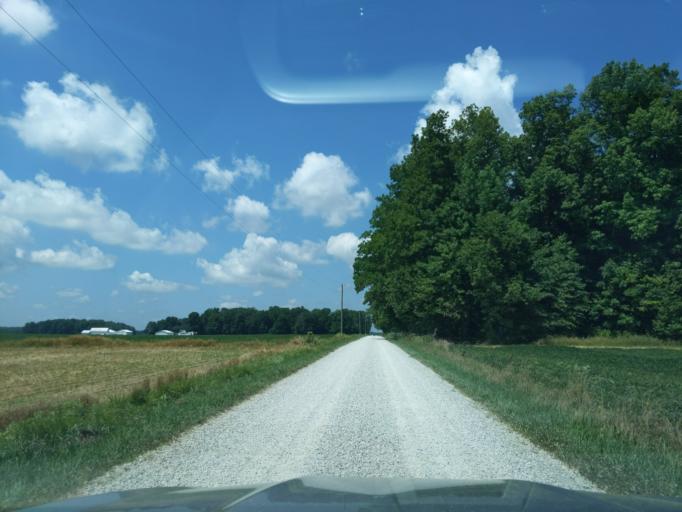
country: US
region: Indiana
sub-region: Ripley County
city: Osgood
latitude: 39.2210
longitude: -85.3561
